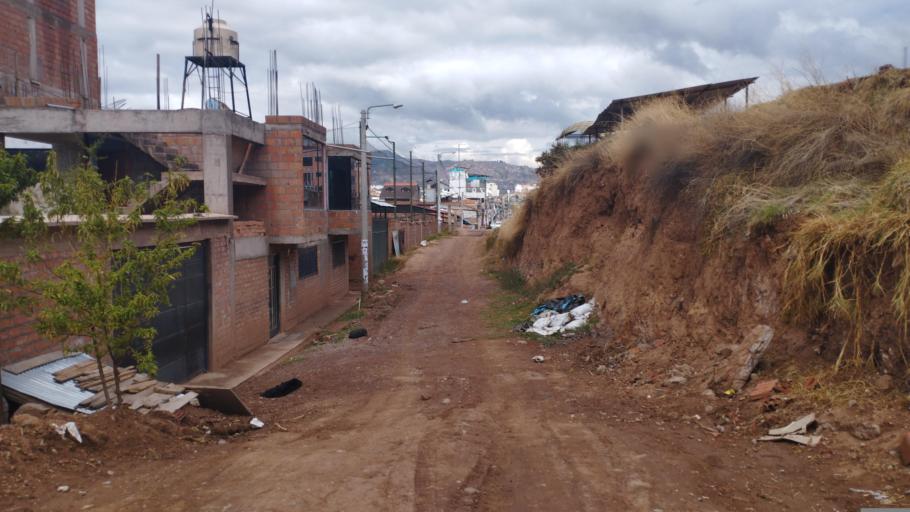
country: PE
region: Cusco
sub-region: Provincia de Cusco
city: Cusco
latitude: -13.5238
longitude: -71.9413
